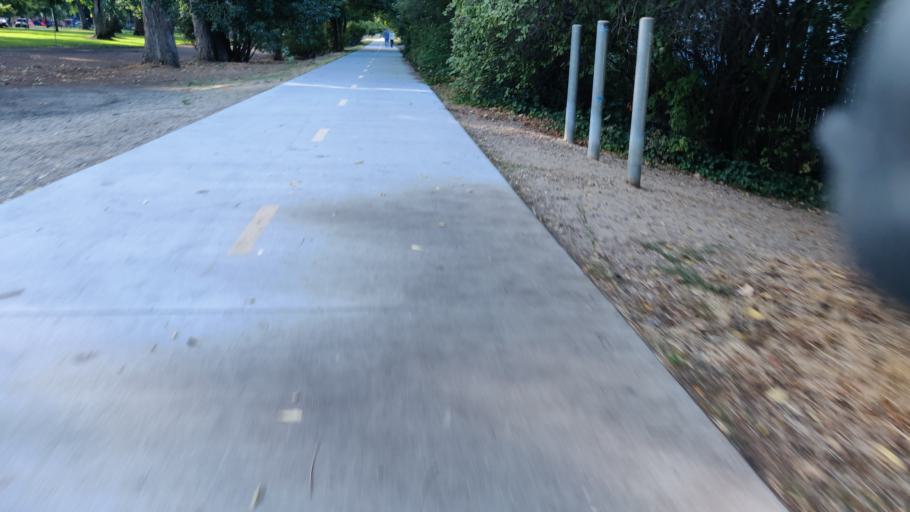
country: US
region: Idaho
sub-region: Ada County
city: Boise
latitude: 43.6026
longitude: -116.1812
